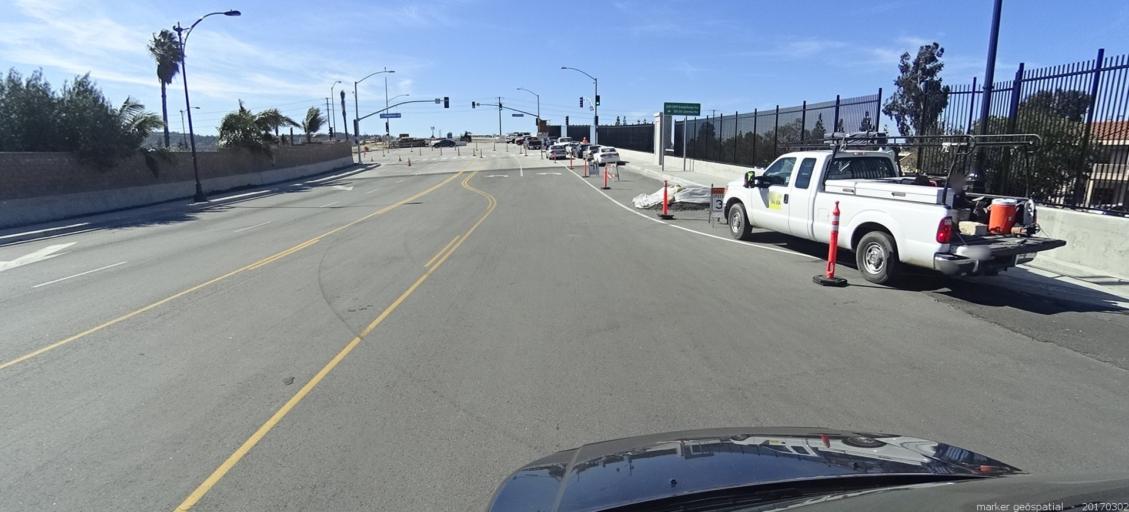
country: US
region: California
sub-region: Orange County
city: Yorba Linda
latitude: 33.8687
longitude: -117.8182
